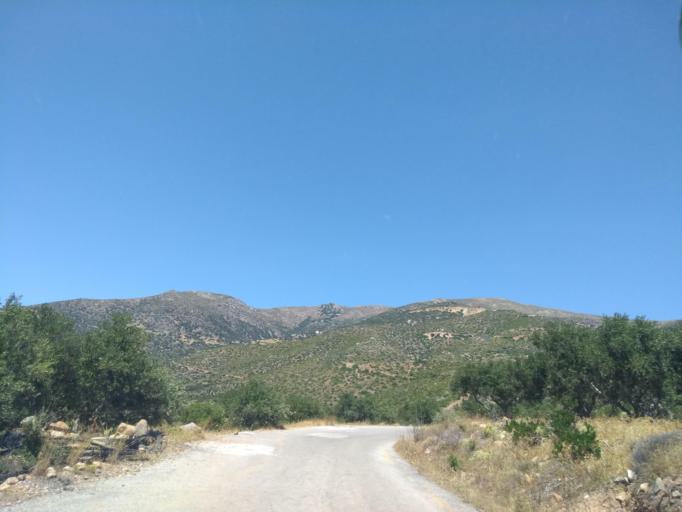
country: GR
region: Crete
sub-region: Nomos Chanias
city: Vryses
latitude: 35.3601
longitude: 23.5413
